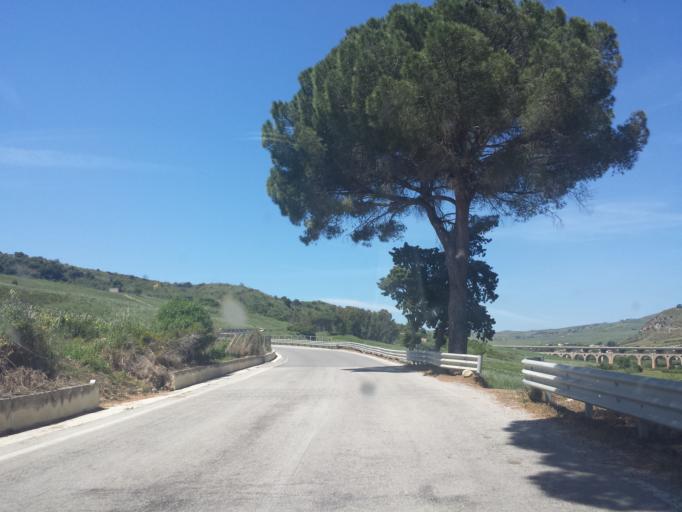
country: IT
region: Sicily
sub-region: Trapani
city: Calatafimi
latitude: 37.9596
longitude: 12.8801
